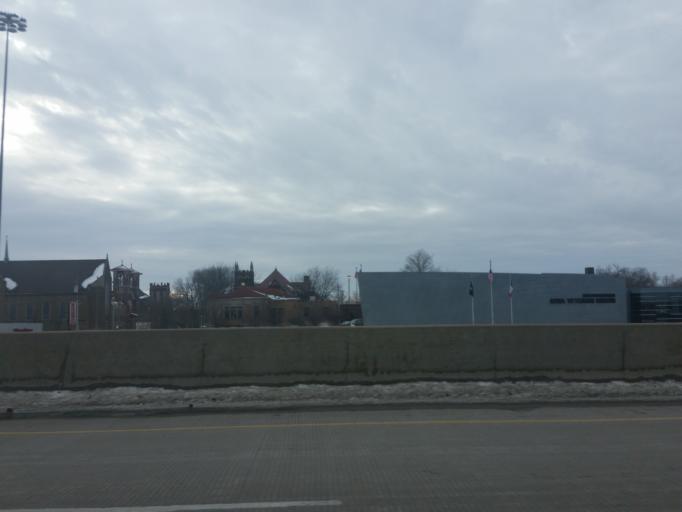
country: US
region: Iowa
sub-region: Black Hawk County
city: Waterloo
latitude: 42.4935
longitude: -92.3424
